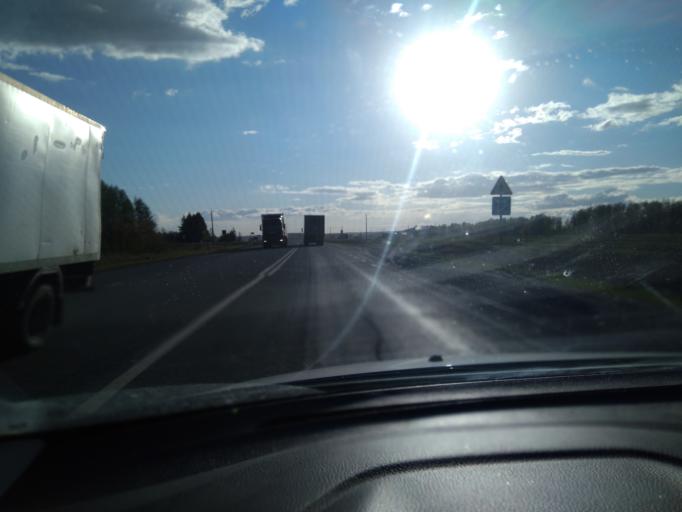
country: RU
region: Sverdlovsk
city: Troitskiy
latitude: 57.0853
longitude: 63.6774
